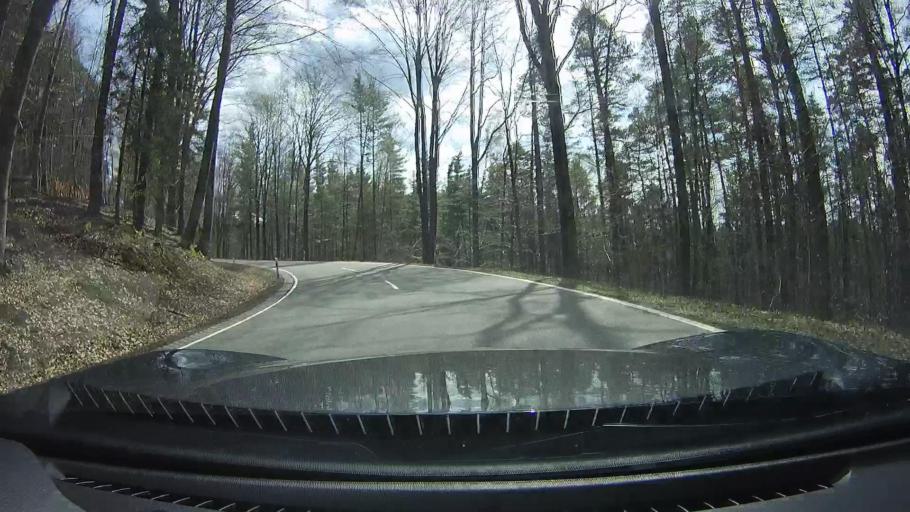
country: DE
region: Hesse
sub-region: Regierungsbezirk Darmstadt
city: Beerfelden
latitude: 49.5849
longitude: 9.0070
